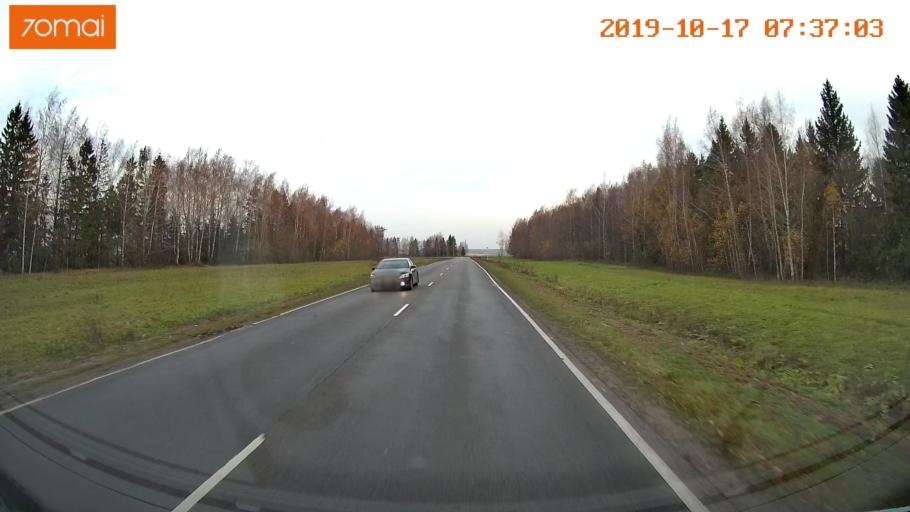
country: RU
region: Vladimir
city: Yur'yev-Pol'skiy
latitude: 56.4457
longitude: 39.9061
